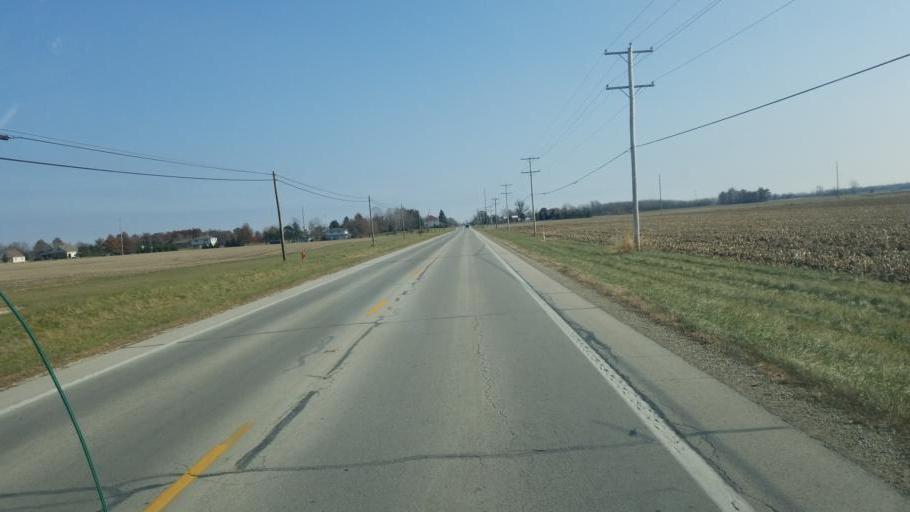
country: US
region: Ohio
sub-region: Mercer County
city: Celina
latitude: 40.5454
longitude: -84.6134
